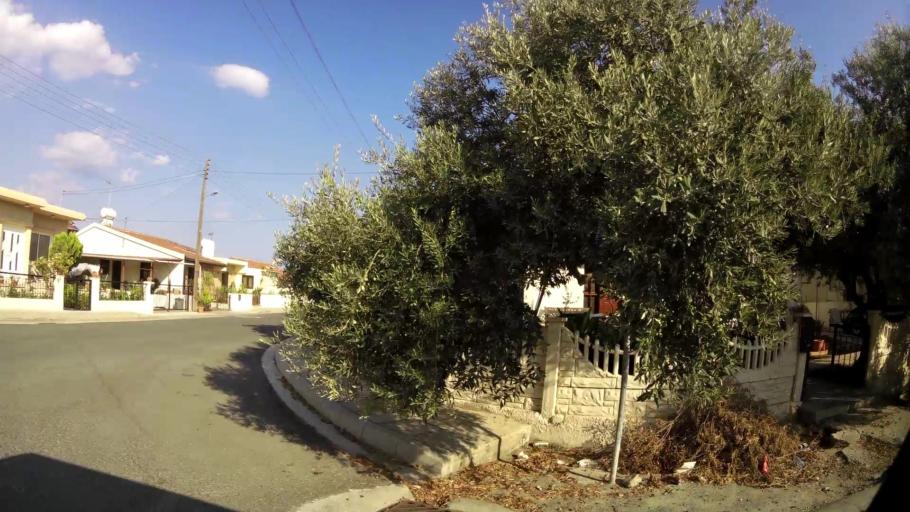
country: CY
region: Larnaka
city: Dhromolaxia
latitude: 34.8746
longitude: 33.5929
